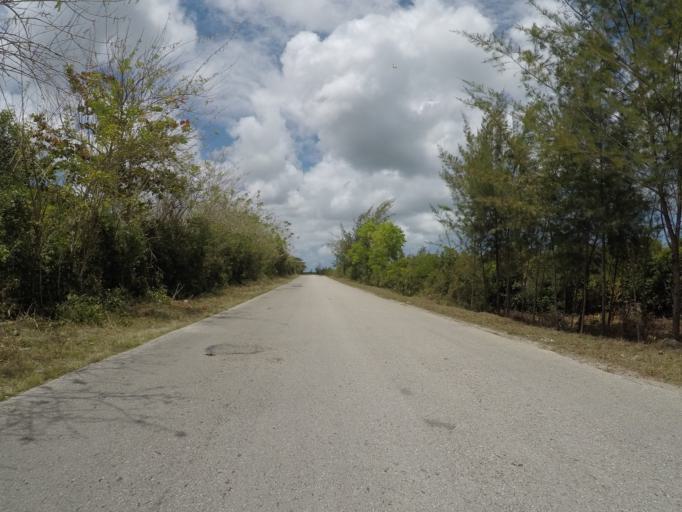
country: TZ
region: Zanzibar Central/South
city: Mahonda
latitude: -6.3282
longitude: 39.4372
